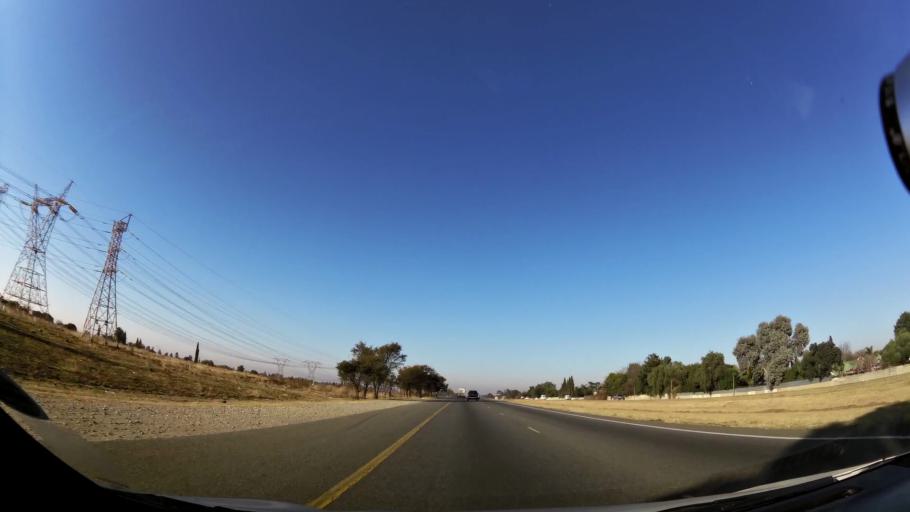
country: ZA
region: Gauteng
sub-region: Ekurhuleni Metropolitan Municipality
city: Germiston
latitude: -26.3142
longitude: 28.1126
